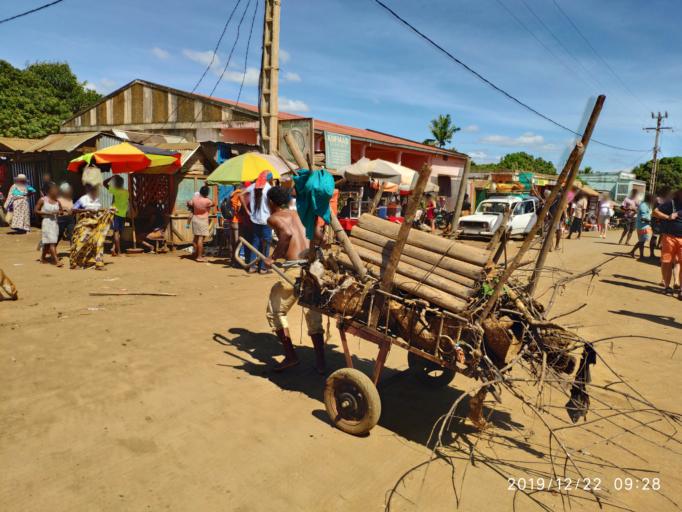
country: MG
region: Diana
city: Sadjoavato
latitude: -12.7418
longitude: 49.2336
